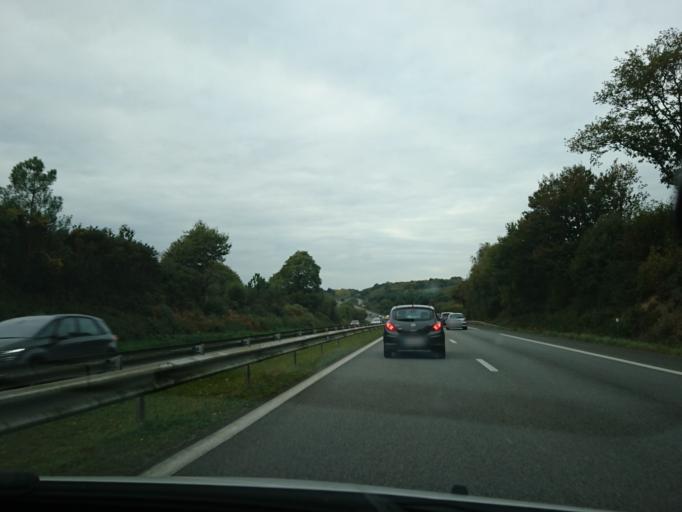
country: FR
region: Brittany
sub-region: Departement du Morbihan
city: Muzillac
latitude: 47.5462
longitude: -2.4394
